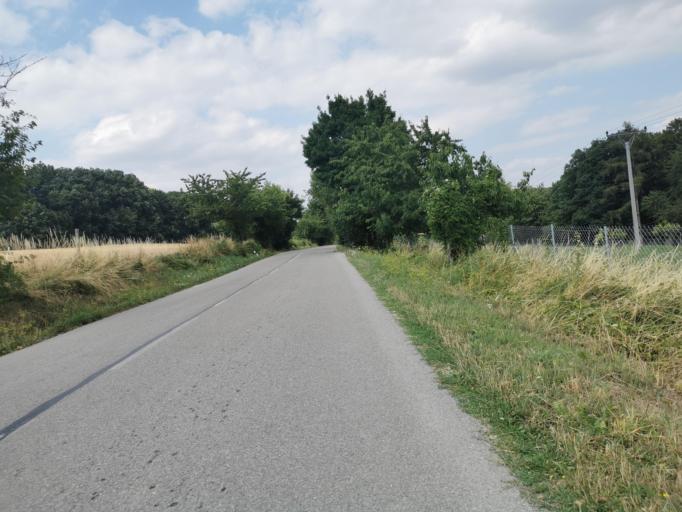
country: SK
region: Nitriansky
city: Brezova pod Bradlom
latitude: 48.7164
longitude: 17.5039
